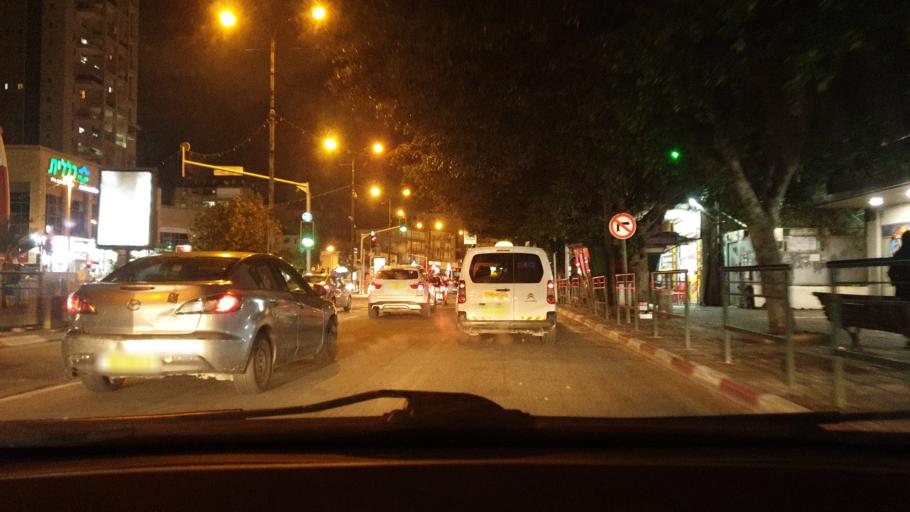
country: IL
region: Central District
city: Rishon LeZiyyon
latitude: 31.9653
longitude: 34.8029
